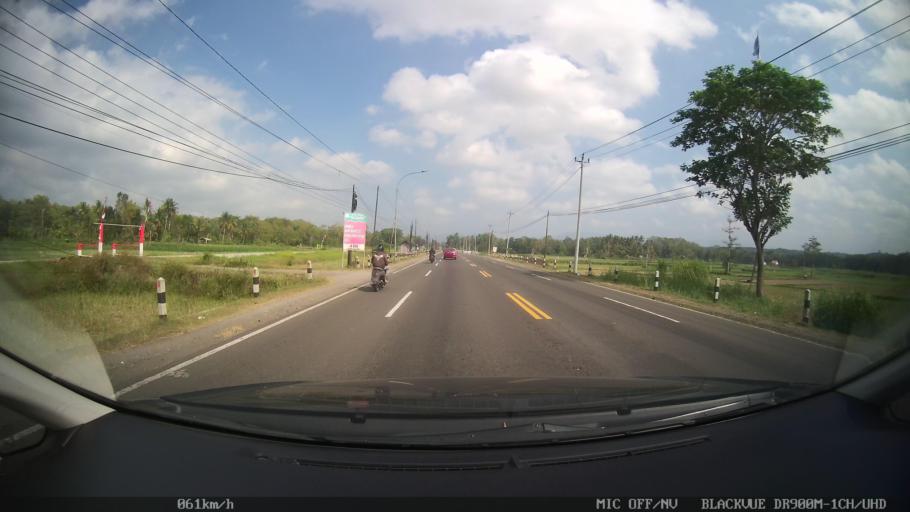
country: ID
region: Daerah Istimewa Yogyakarta
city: Srandakan
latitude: -7.8745
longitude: 110.2025
